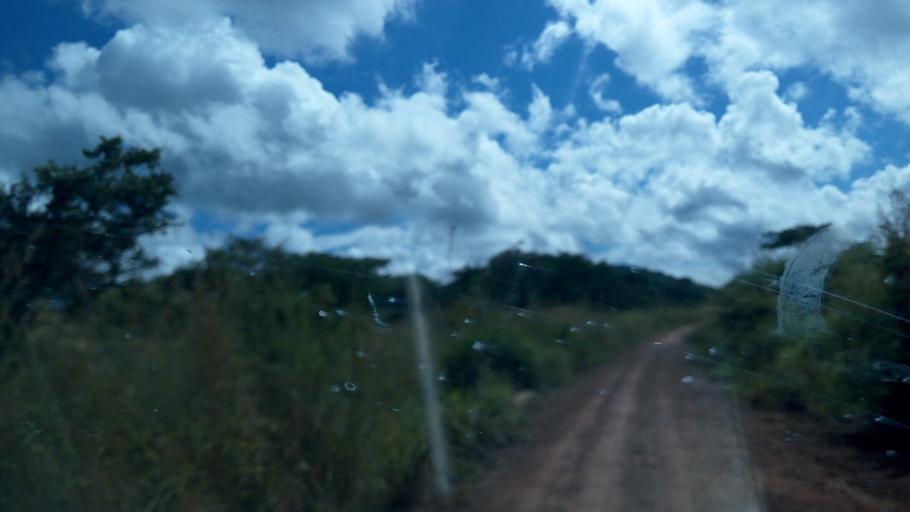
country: ZM
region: Northern
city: Kaputa
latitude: -8.2269
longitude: 29.0464
